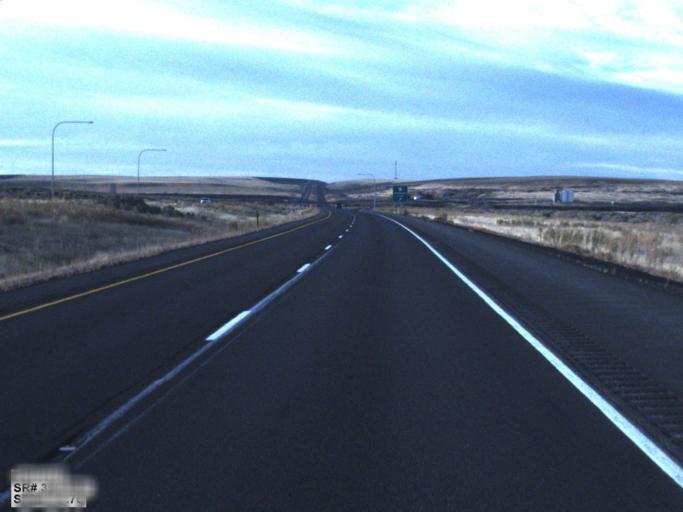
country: US
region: Washington
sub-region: Adams County
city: Ritzville
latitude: 46.9784
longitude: -118.5649
